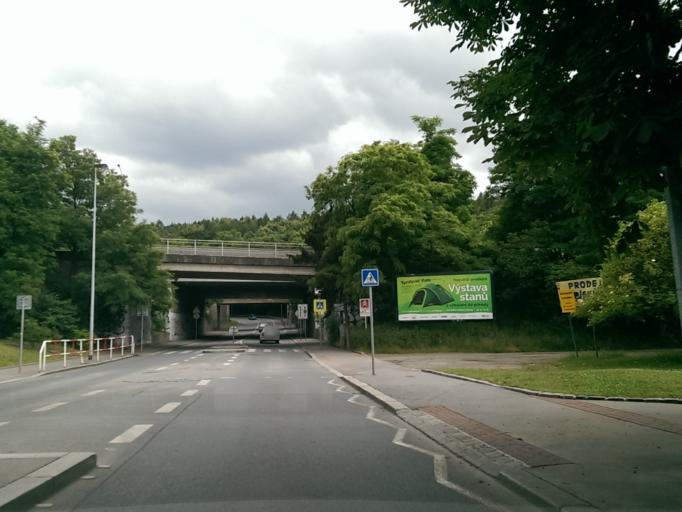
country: CZ
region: Praha
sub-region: Praha 4
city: Hodkovicky
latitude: 50.0326
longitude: 14.4161
